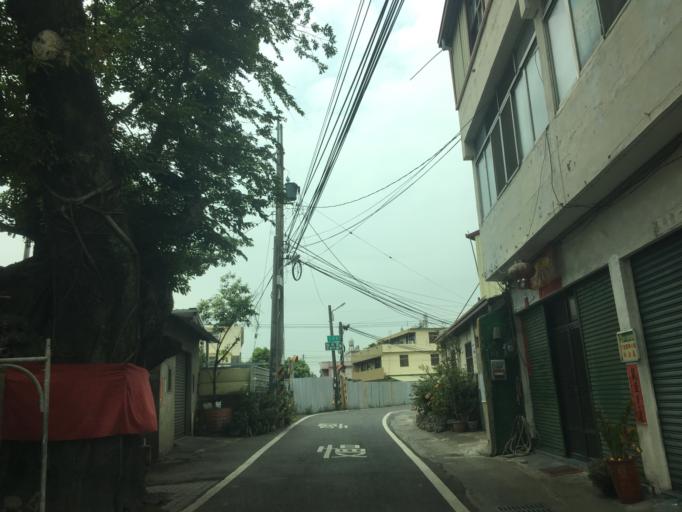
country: TW
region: Taiwan
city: Zhongxing New Village
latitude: 24.0382
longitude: 120.6882
